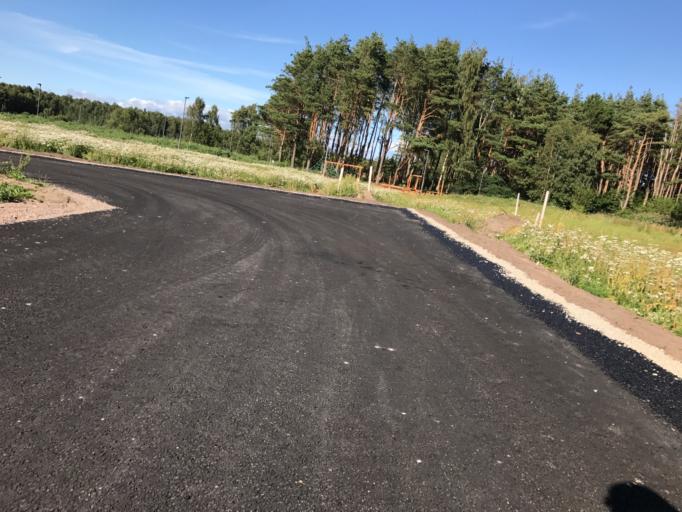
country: SE
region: Skane
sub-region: Bastads Kommun
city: Bastad
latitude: 56.4422
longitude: 12.9095
